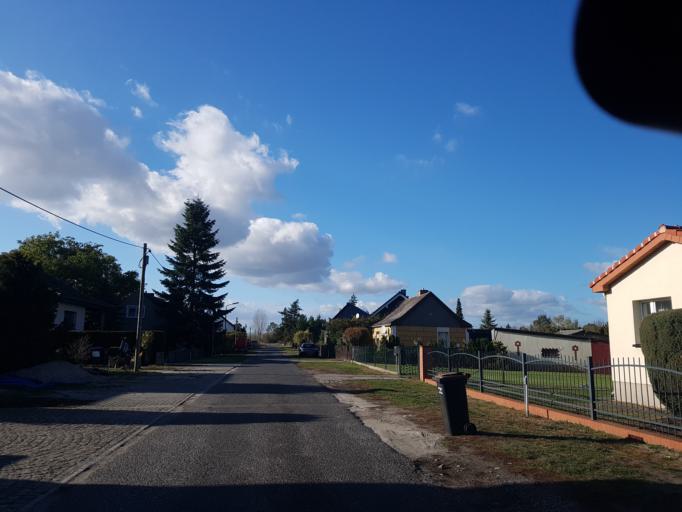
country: DE
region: Brandenburg
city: Nauen
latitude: 52.6365
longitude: 12.9025
